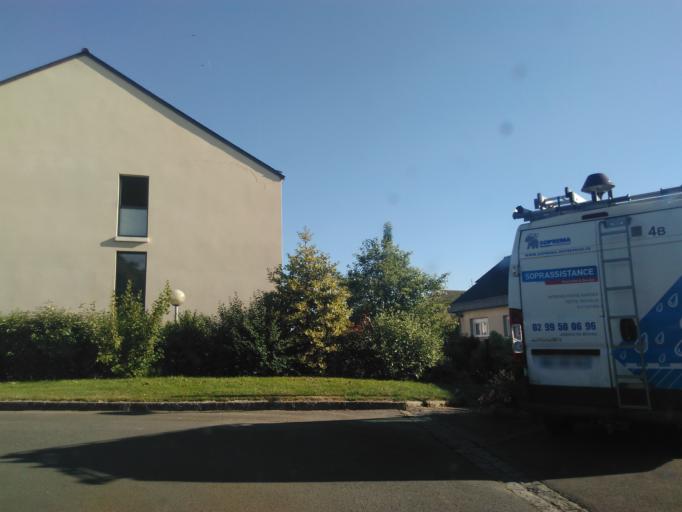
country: FR
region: Brittany
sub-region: Departement d'Ille-et-Vilaine
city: La Meziere
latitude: 48.2190
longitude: -1.7545
